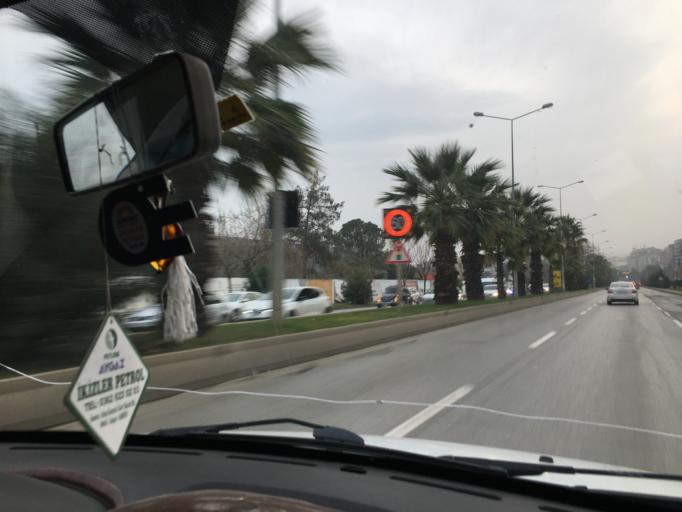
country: TR
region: Samsun
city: Samsun
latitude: 41.3080
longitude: 36.3341
